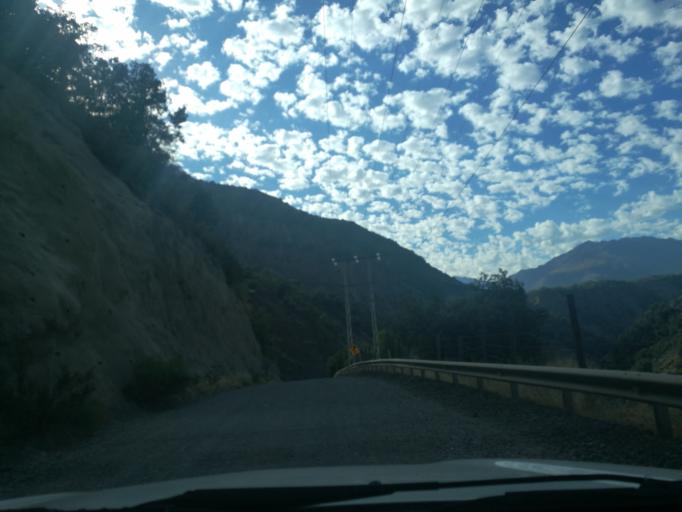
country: CL
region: O'Higgins
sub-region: Provincia de Cachapoal
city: Machali
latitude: -34.2795
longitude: -70.4460
